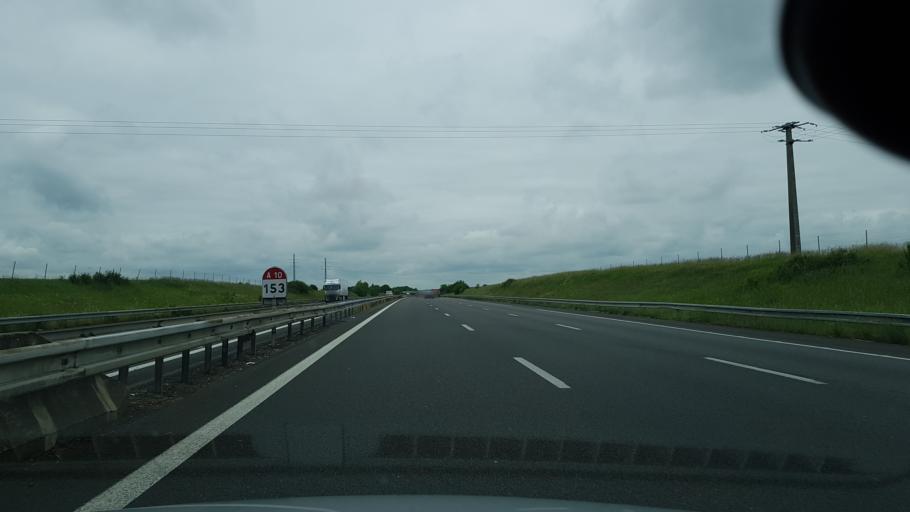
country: FR
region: Centre
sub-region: Departement du Loir-et-Cher
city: Villebarou
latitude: 47.6161
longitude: 1.2929
